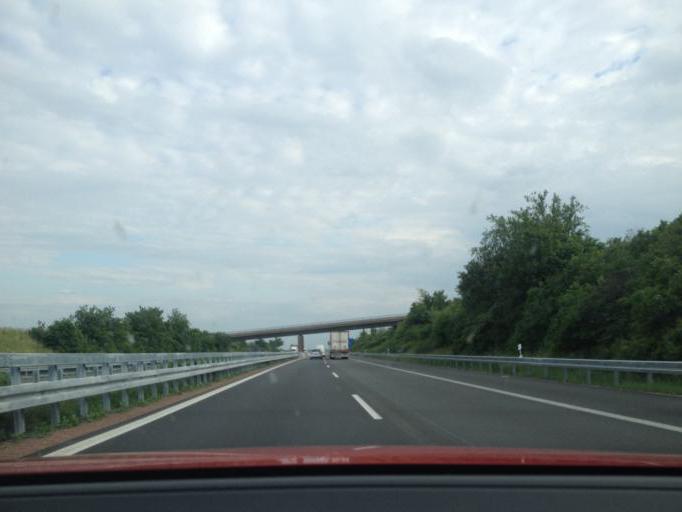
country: DE
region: Saxony-Anhalt
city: Oppin
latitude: 51.5520
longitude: 12.0080
